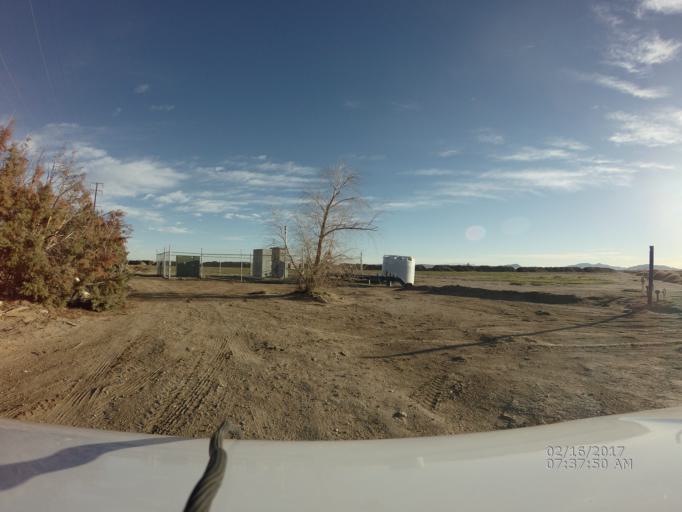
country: US
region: California
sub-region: Los Angeles County
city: Littlerock
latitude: 34.6682
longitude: -117.9696
